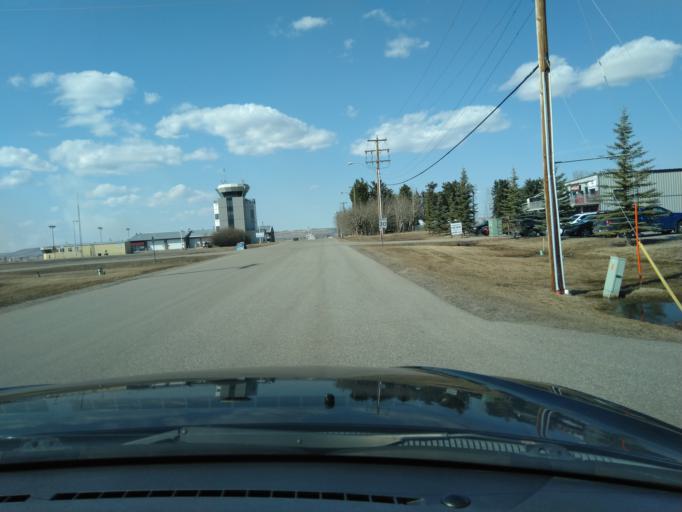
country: CA
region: Alberta
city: Cochrane
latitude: 51.1011
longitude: -114.3737
